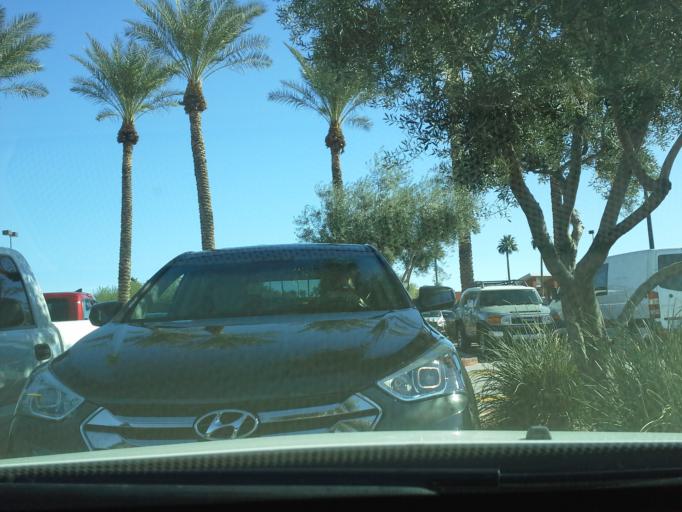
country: US
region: Arizona
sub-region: Maricopa County
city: Guadalupe
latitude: 33.3399
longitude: -111.9706
